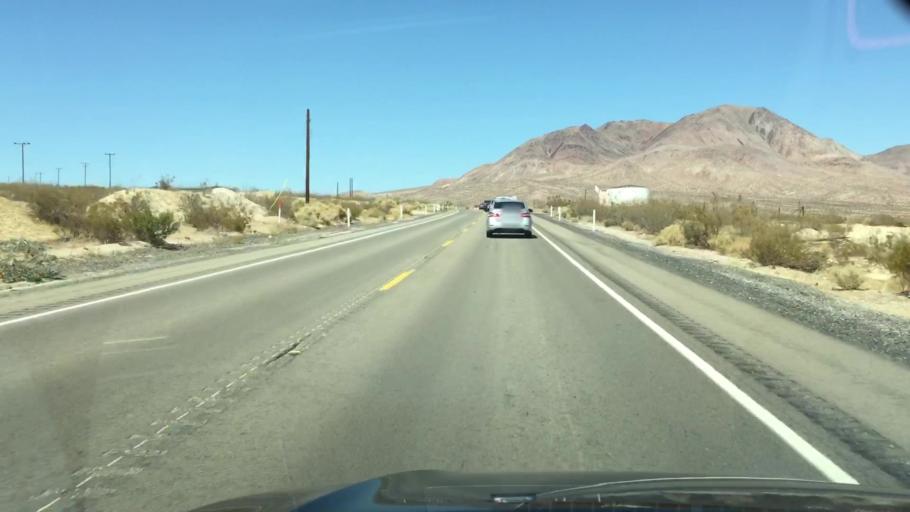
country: US
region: California
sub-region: Kern County
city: Boron
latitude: 35.3126
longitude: -117.6097
